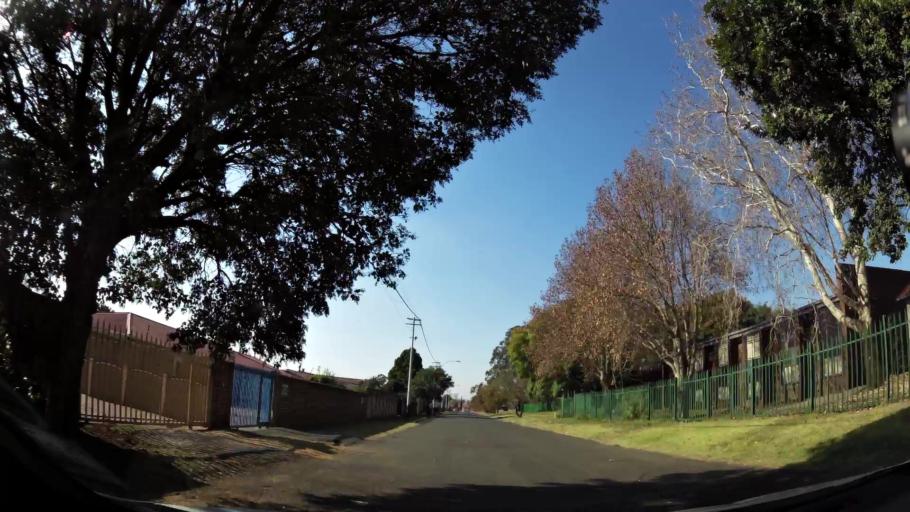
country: ZA
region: Gauteng
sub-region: City of Johannesburg Metropolitan Municipality
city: Johannesburg
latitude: -26.2485
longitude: 28.0037
